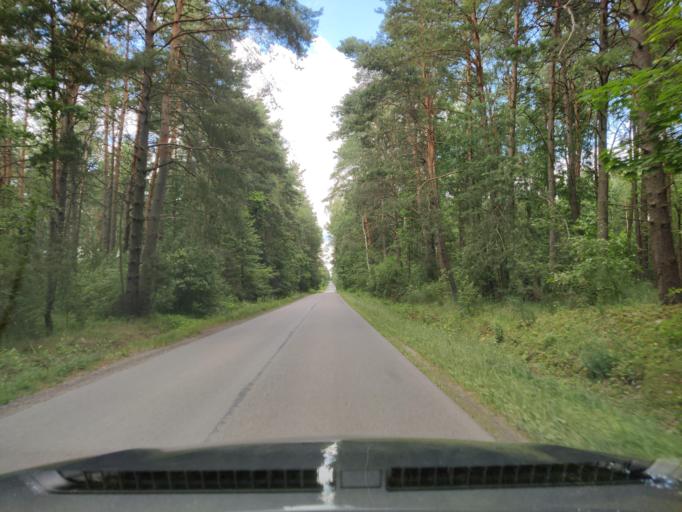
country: PL
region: Masovian Voivodeship
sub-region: Powiat wegrowski
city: Miedzna
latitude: 52.5305
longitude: 22.0798
